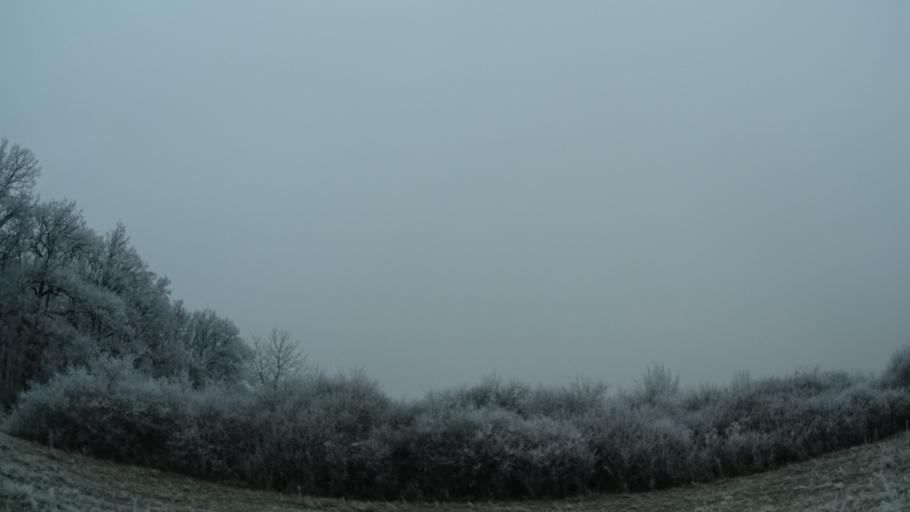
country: DE
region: Bavaria
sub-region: Regierungsbezirk Unterfranken
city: Hassfurt
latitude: 50.0642
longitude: 10.5463
